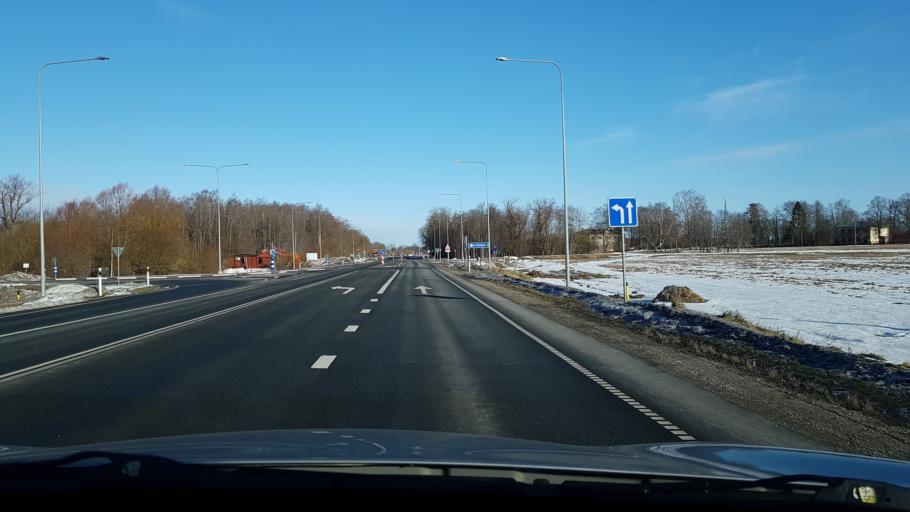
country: EE
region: Viljandimaa
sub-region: Vohma linn
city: Vohma
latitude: 58.6276
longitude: 25.5704
